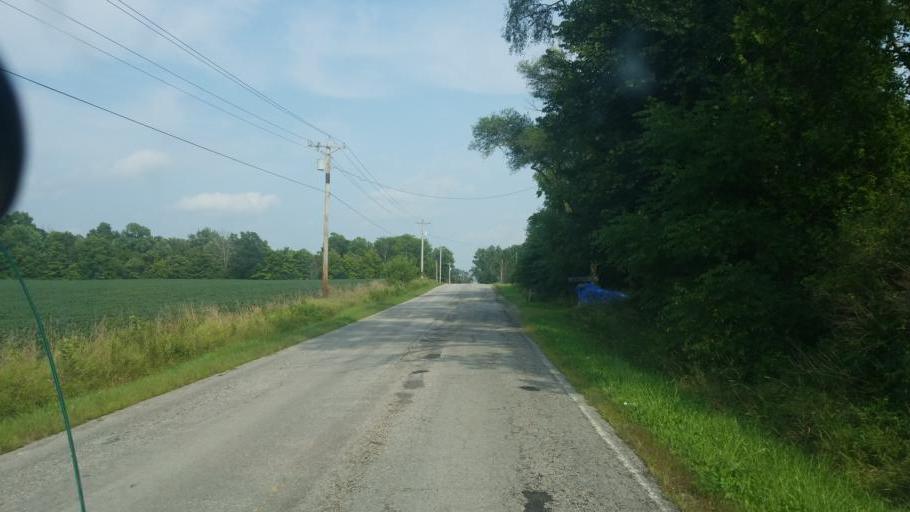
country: US
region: Ohio
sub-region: Medina County
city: Lodi
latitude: 41.1361
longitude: -82.0368
